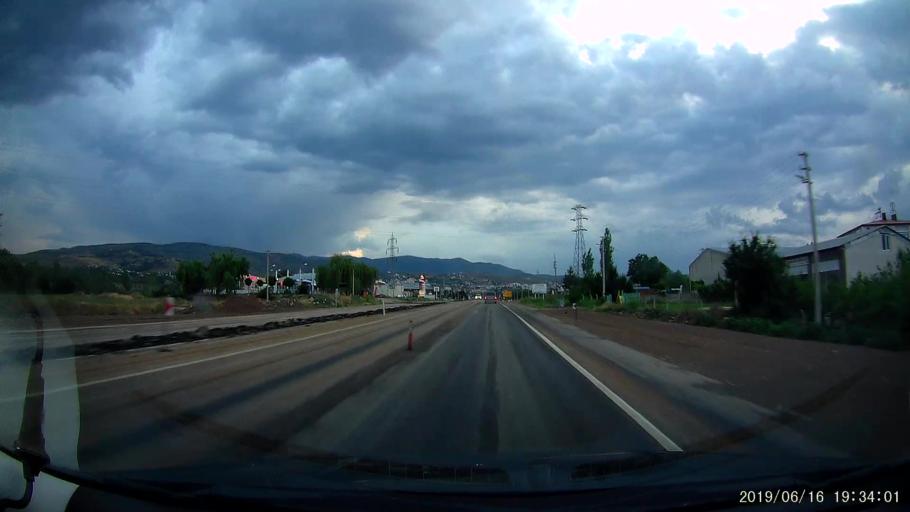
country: TR
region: Sivas
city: Susehri
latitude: 40.1707
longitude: 38.1145
